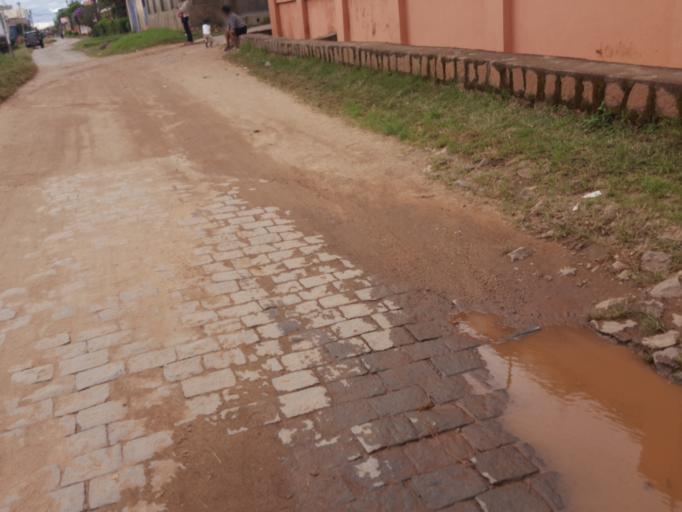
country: MG
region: Analamanga
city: Antananarivo
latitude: -18.8923
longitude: 47.5414
